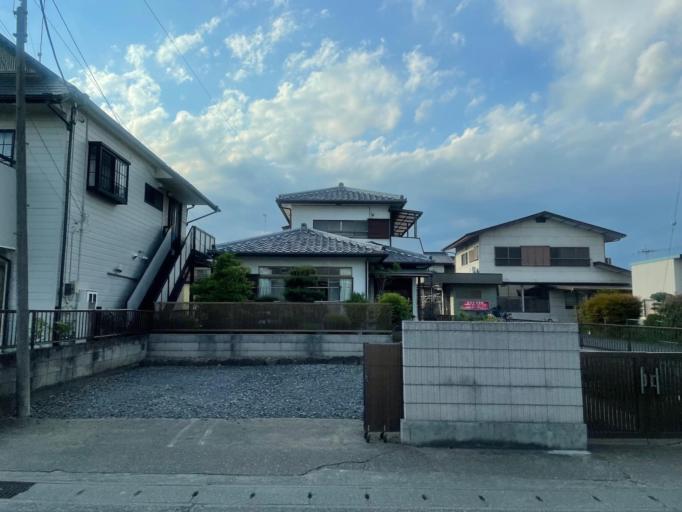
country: JP
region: Tochigi
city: Tochigi
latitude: 36.3776
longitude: 139.7236
